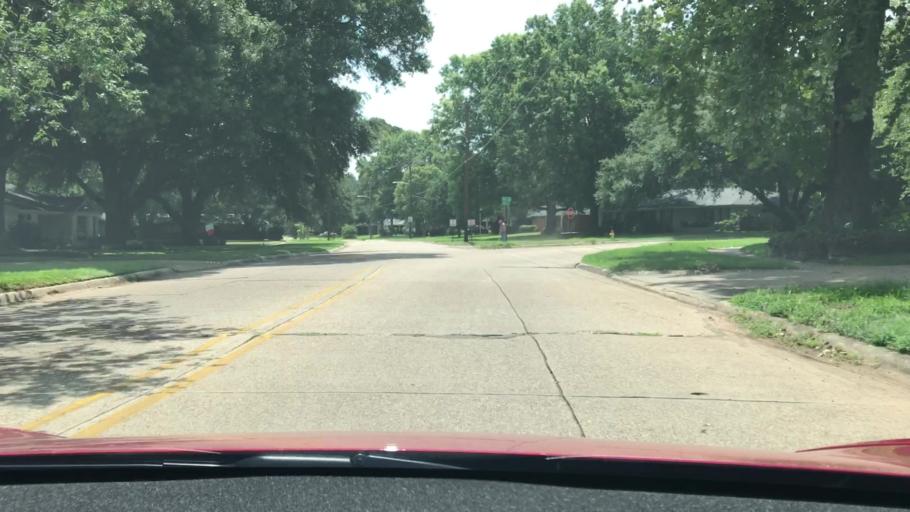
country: US
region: Louisiana
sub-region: Bossier Parish
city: Bossier City
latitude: 32.4584
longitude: -93.7330
